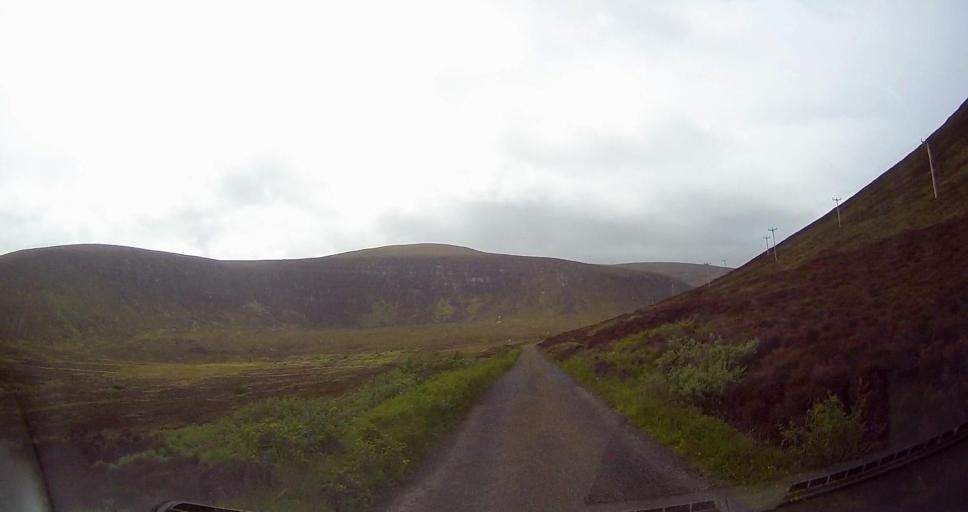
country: GB
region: Scotland
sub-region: Orkney Islands
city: Stromness
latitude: 58.8942
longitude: -3.3144
